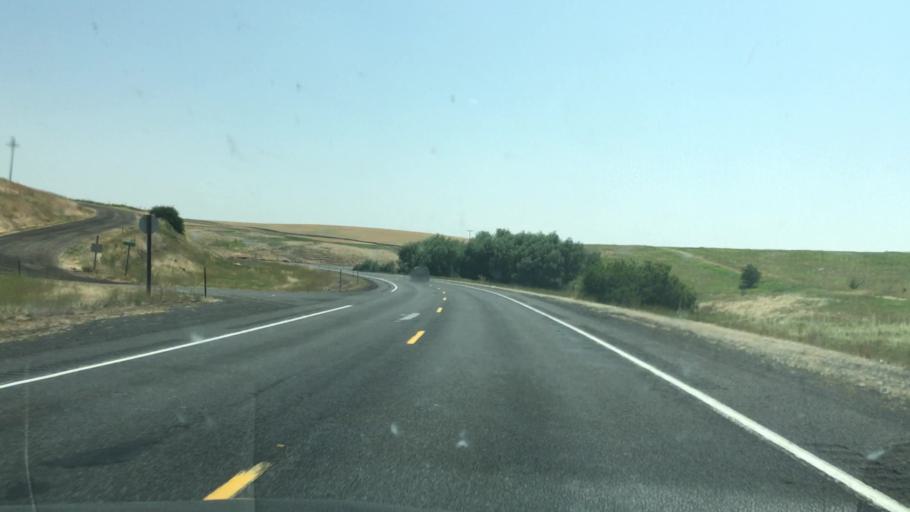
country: US
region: Idaho
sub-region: Lewis County
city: Nezperce
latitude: 46.2200
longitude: -116.4344
